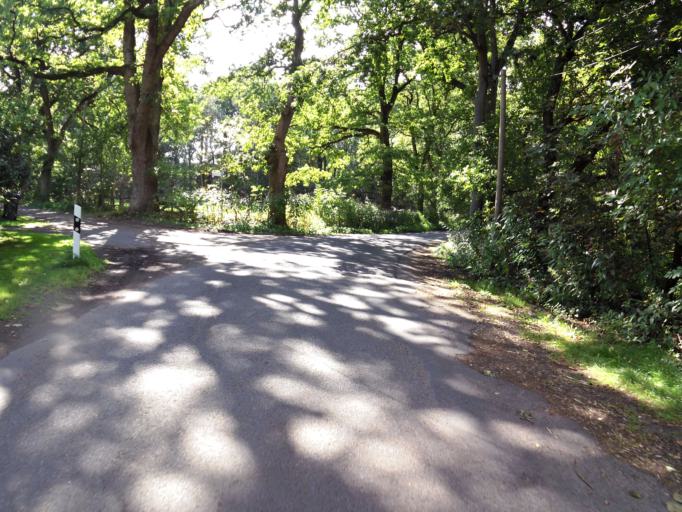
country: DE
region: Lower Saxony
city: Seedorf
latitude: 53.3337
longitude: 9.2000
